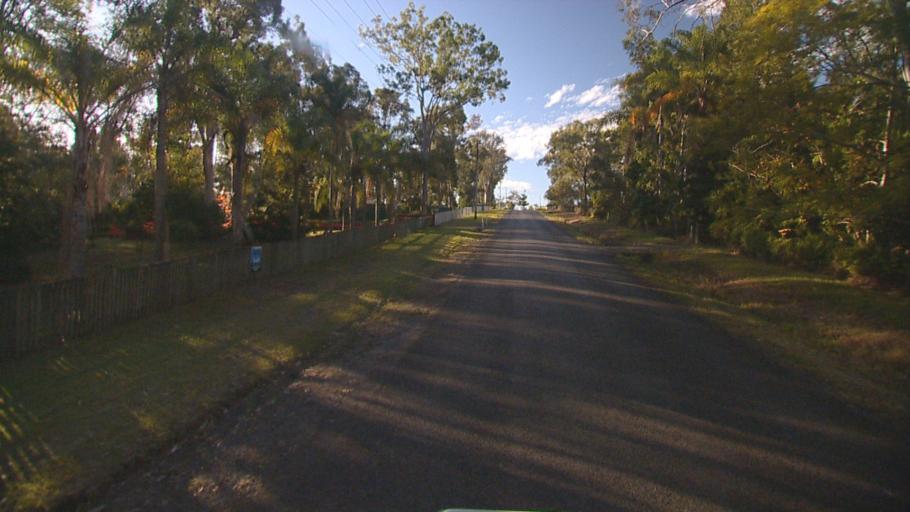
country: AU
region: Queensland
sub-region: Logan
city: Waterford West
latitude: -27.7219
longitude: 153.1538
